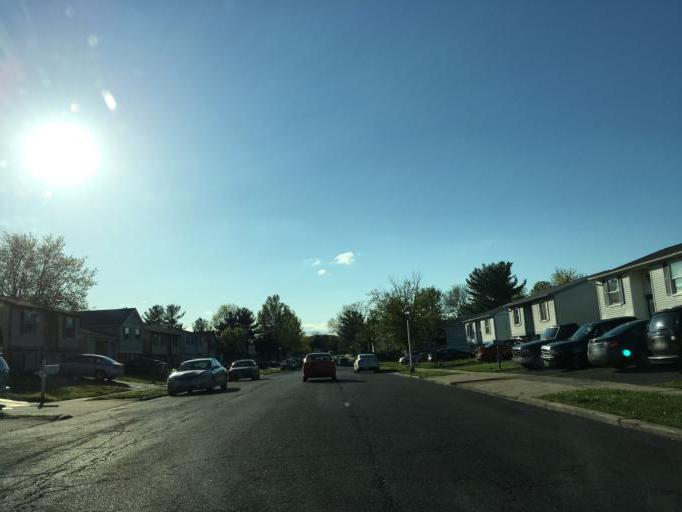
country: US
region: Maryland
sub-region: Frederick County
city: Frederick
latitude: 39.4026
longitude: -77.4242
